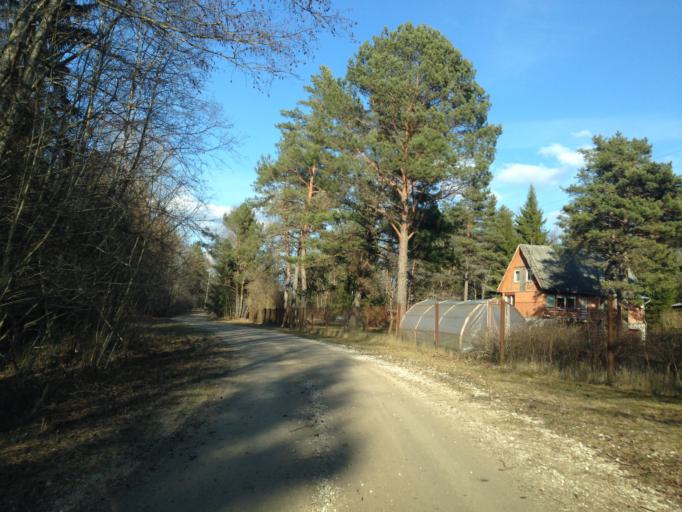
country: EE
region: Harju
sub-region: Nissi vald
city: Turba
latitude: 59.1344
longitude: 24.1703
